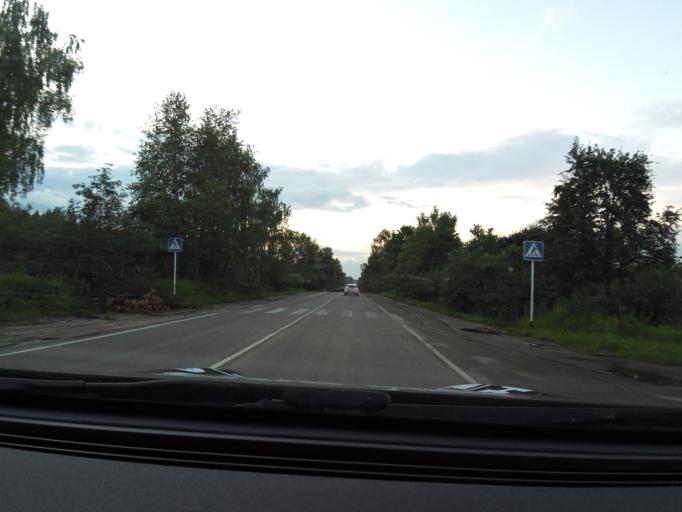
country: RU
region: Vladimir
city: Kol'chugino
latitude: 56.2921
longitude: 39.3332
